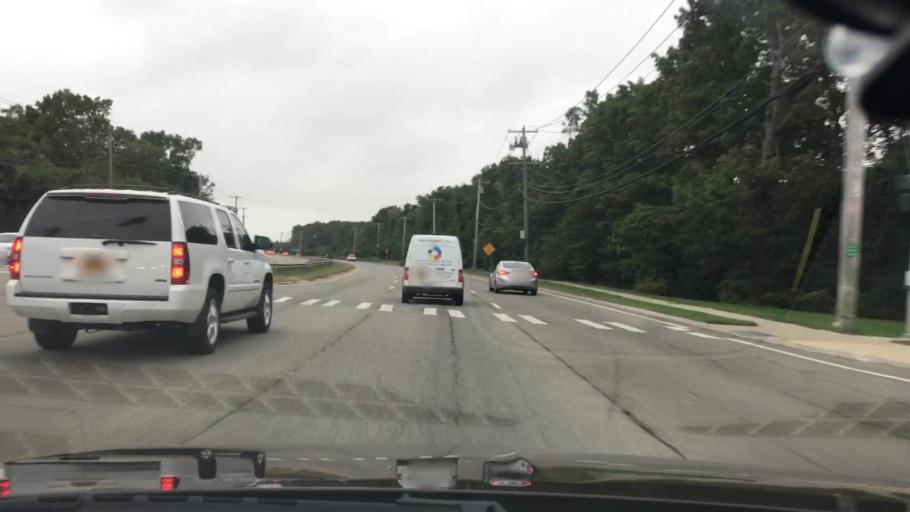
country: US
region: New York
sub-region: Suffolk County
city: Nesconset
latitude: 40.8668
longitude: -73.1353
